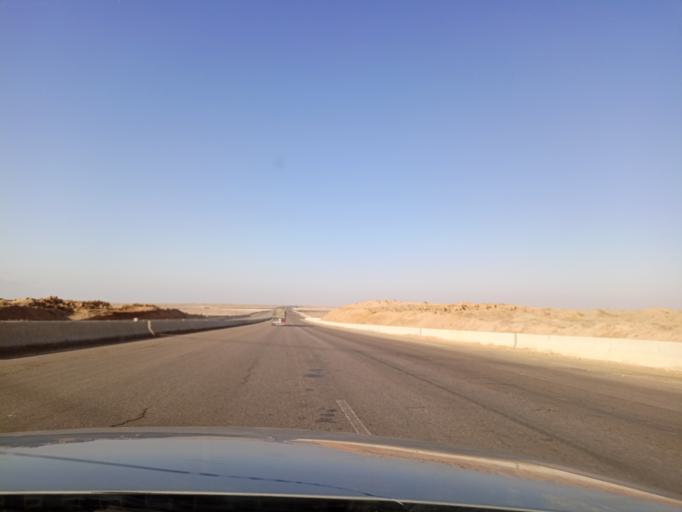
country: EG
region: Muhafazat al Fayyum
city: Tamiyah
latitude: 29.6293
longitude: 30.9669
